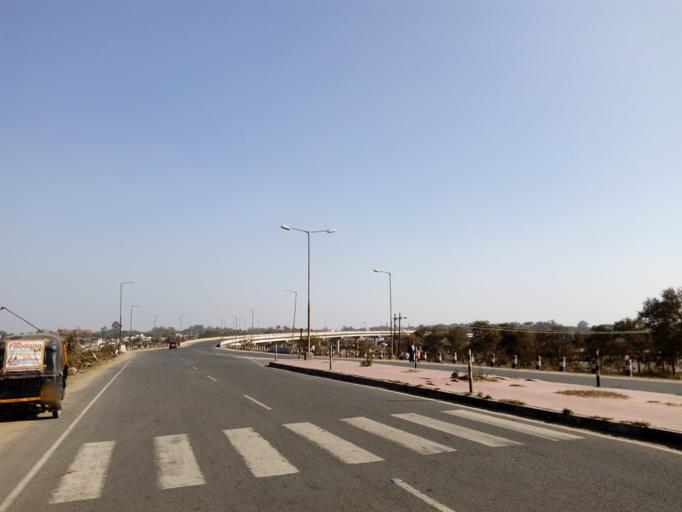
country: IN
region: Jharkhand
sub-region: Ranchi
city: Ranchi
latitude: 23.3548
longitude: 85.3682
